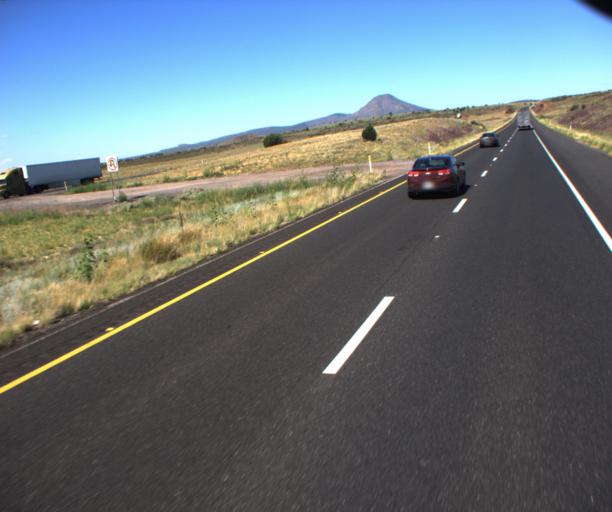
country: US
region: Arizona
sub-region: Yavapai County
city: Paulden
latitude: 35.2359
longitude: -112.6366
